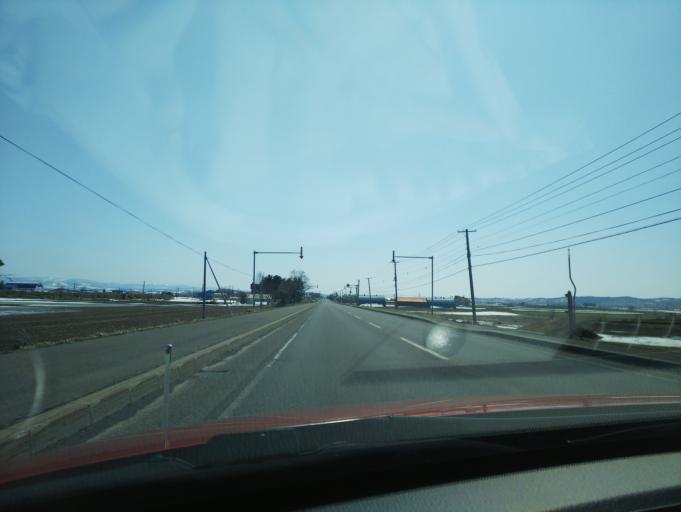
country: JP
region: Hokkaido
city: Nayoro
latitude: 44.2341
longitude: 142.3948
